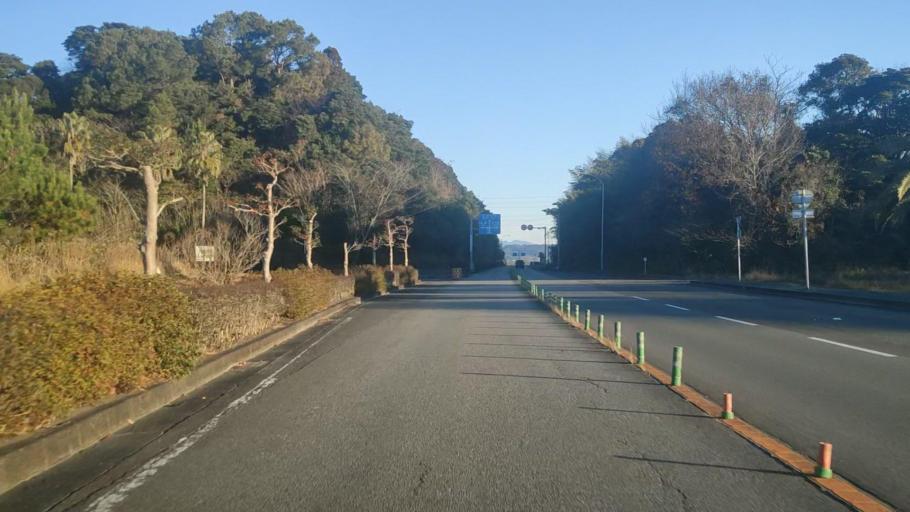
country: JP
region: Miyazaki
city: Tsuma
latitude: 32.0293
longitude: 131.4642
